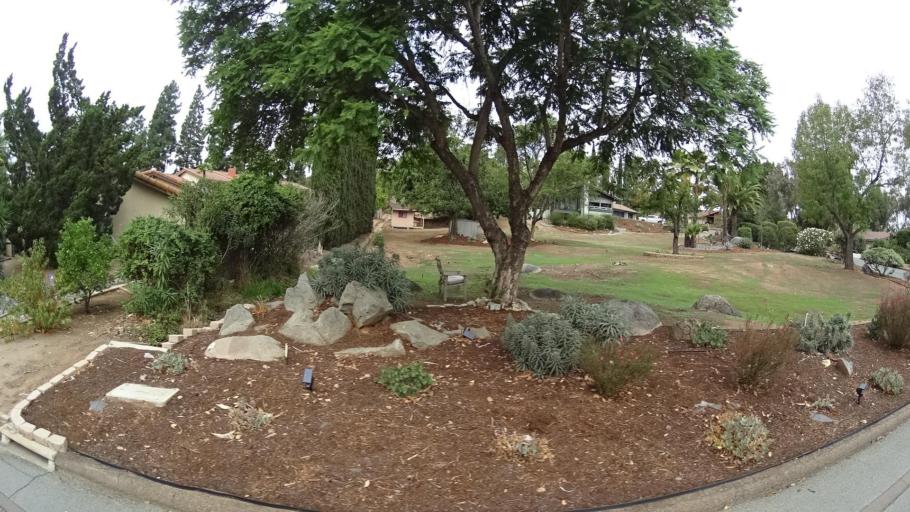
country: US
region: California
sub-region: San Diego County
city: Granite Hills
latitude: 32.7748
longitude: -116.9177
